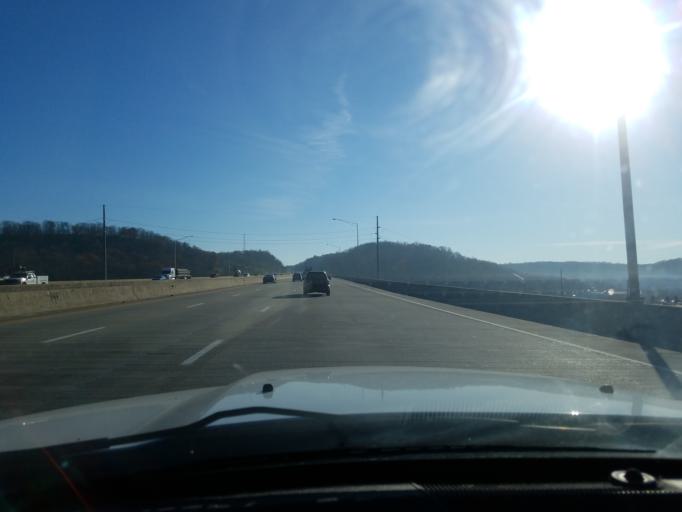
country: US
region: Kentucky
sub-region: Kenton County
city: Fort Wright
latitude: 39.0287
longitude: -84.5351
